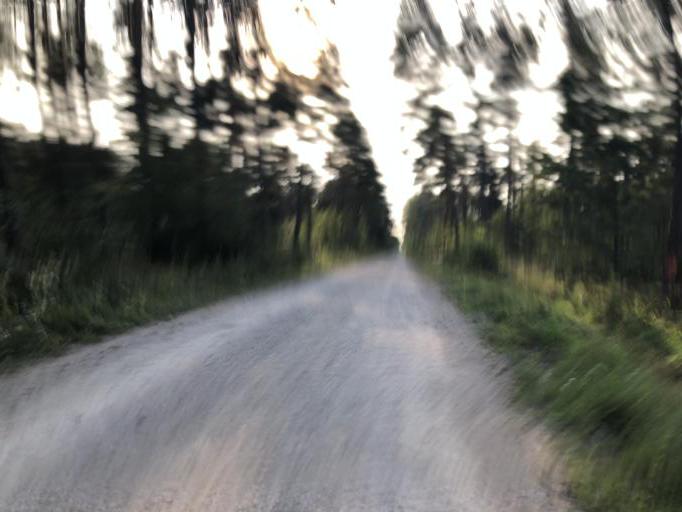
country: DE
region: Bavaria
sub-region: Regierungsbezirk Mittelfranken
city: Uttenreuth
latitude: 49.5789
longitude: 11.0818
